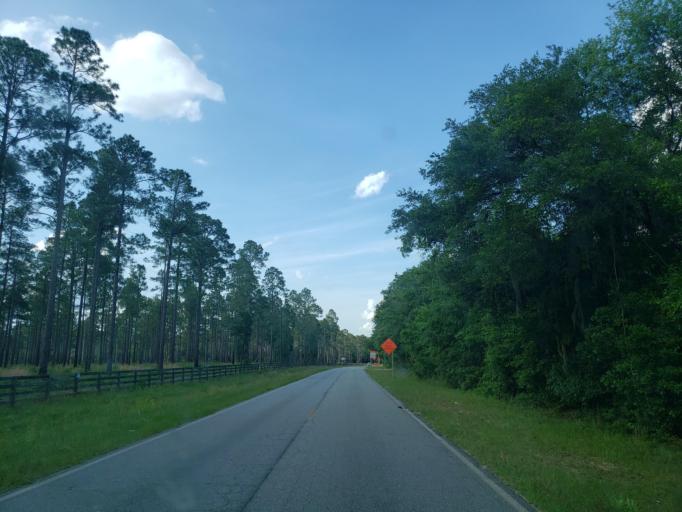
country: US
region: Georgia
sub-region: Echols County
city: Statenville
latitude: 30.6358
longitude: -83.1951
